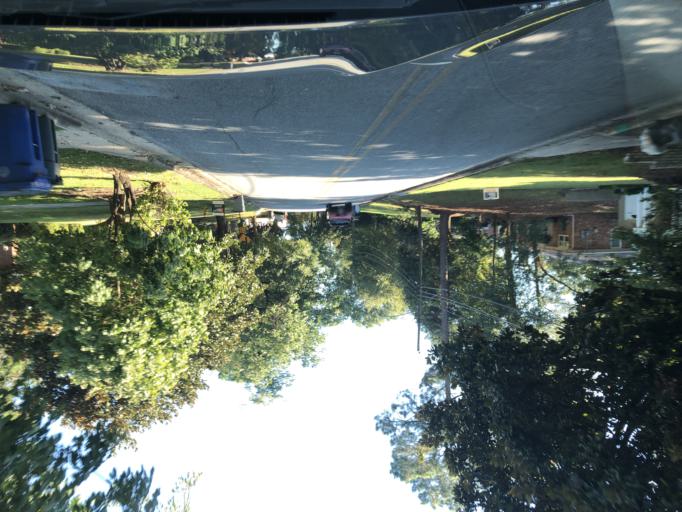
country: US
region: Georgia
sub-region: Muscogee County
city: Columbus
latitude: 32.4799
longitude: -84.9474
